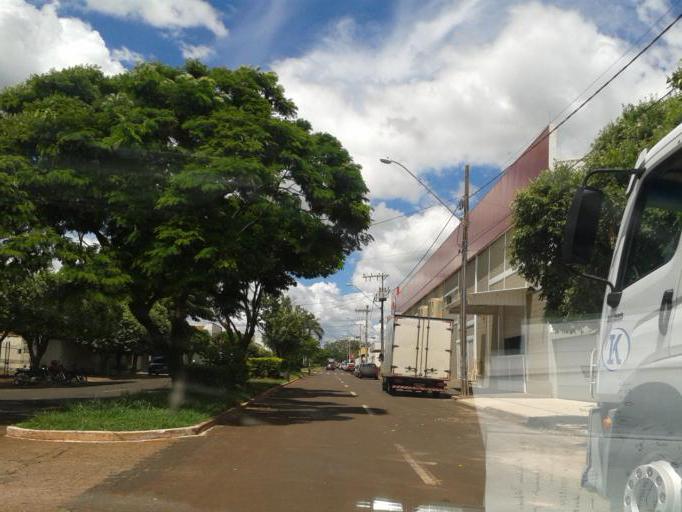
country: BR
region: Minas Gerais
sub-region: Santa Vitoria
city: Santa Vitoria
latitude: -18.8409
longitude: -50.1219
